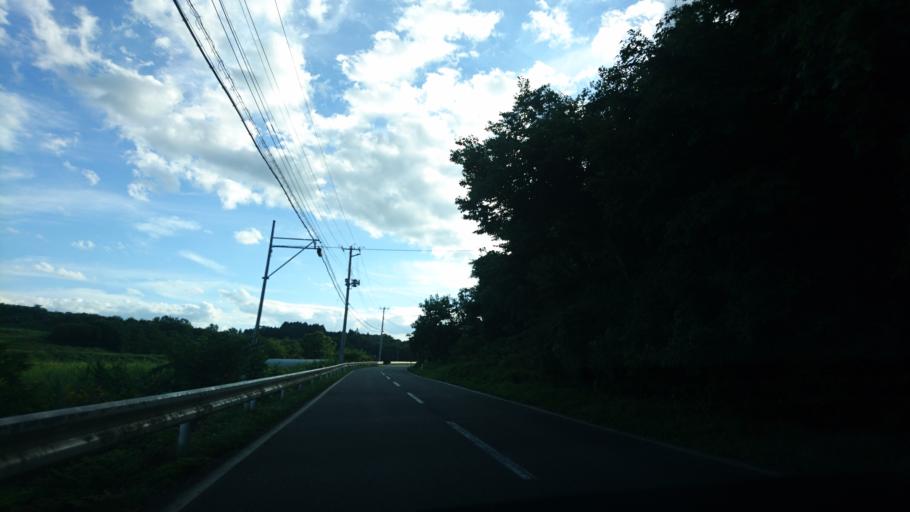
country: JP
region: Iwate
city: Ichinoseki
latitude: 38.8352
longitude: 141.1251
